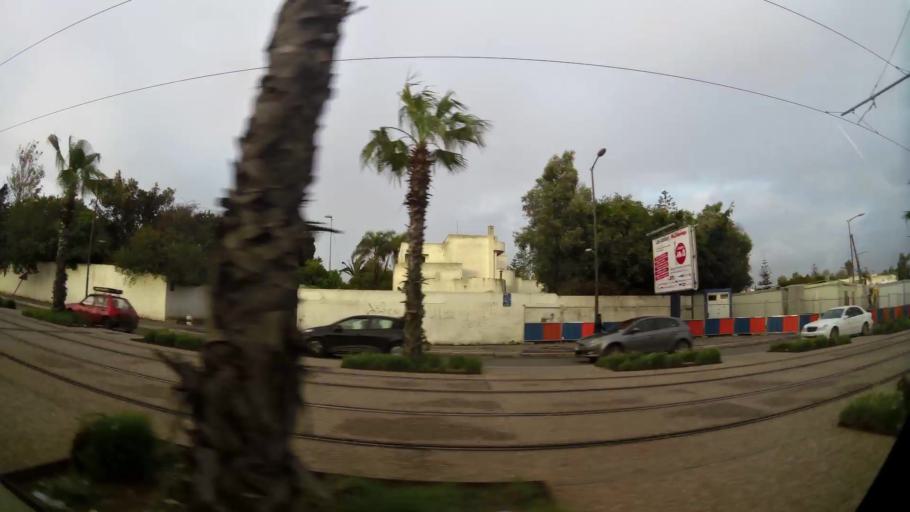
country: MA
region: Grand Casablanca
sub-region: Casablanca
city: Casablanca
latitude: 33.5780
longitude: -7.6739
